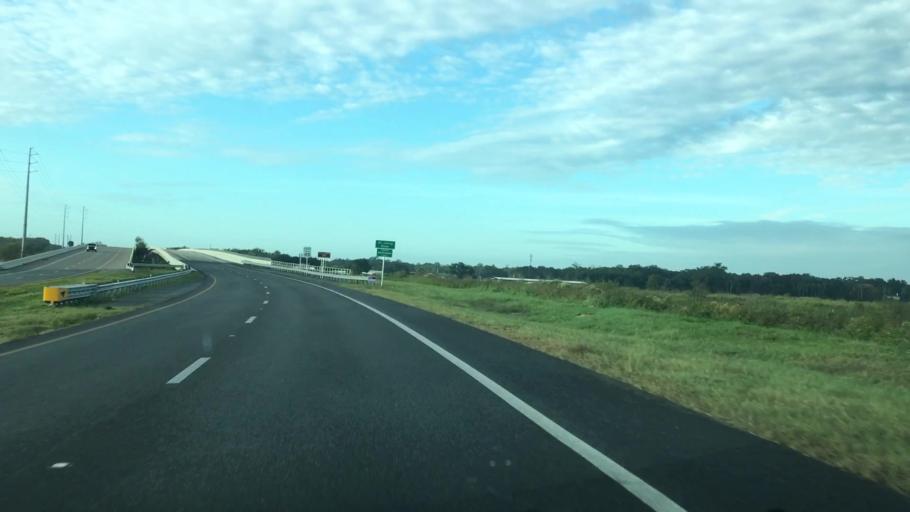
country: US
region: Florida
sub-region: Seminole County
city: Midway
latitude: 28.8067
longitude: -81.2081
